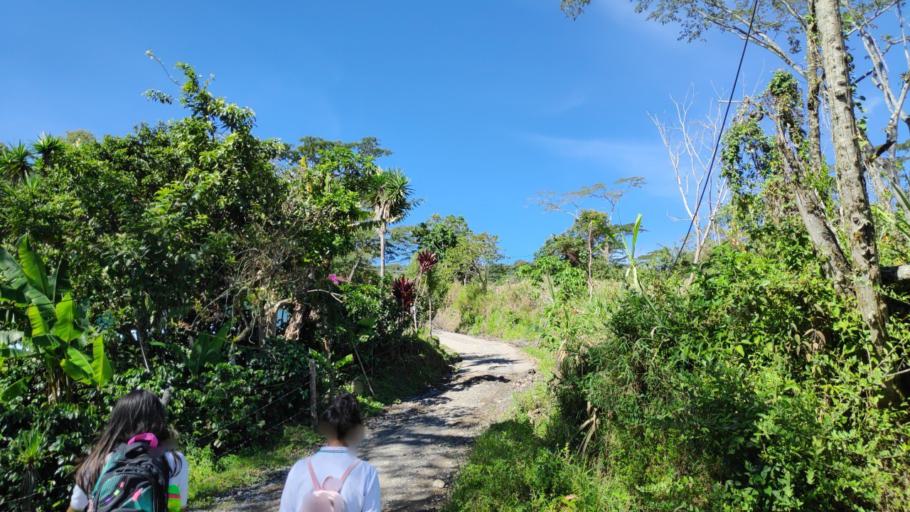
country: CO
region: Santander
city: Guepsa
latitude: 5.9887
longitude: -73.5430
